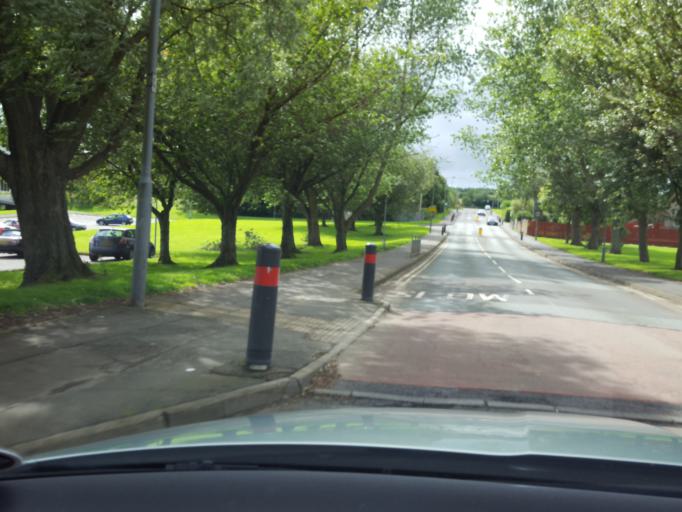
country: GB
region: Scotland
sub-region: Falkirk
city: Bo'ness
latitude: 56.0087
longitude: -3.5999
